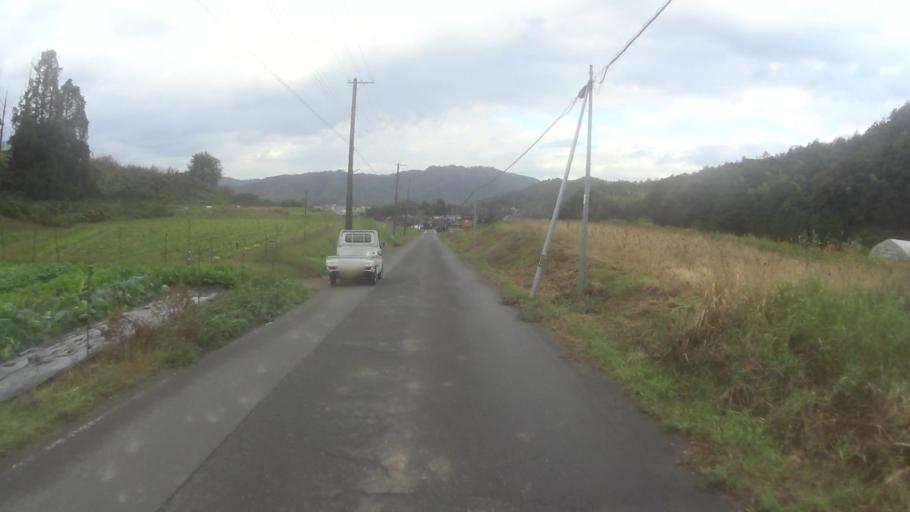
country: JP
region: Kyoto
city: Miyazu
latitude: 35.5180
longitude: 135.1257
